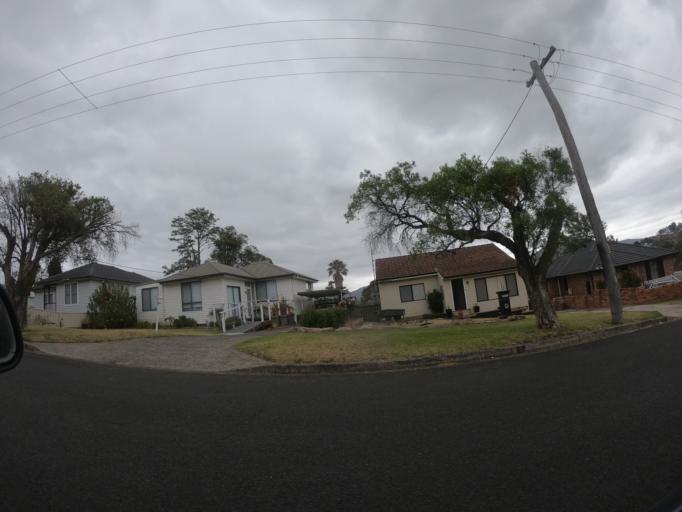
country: AU
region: New South Wales
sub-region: Wollongong
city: Berkeley
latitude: -34.4795
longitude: 150.8402
